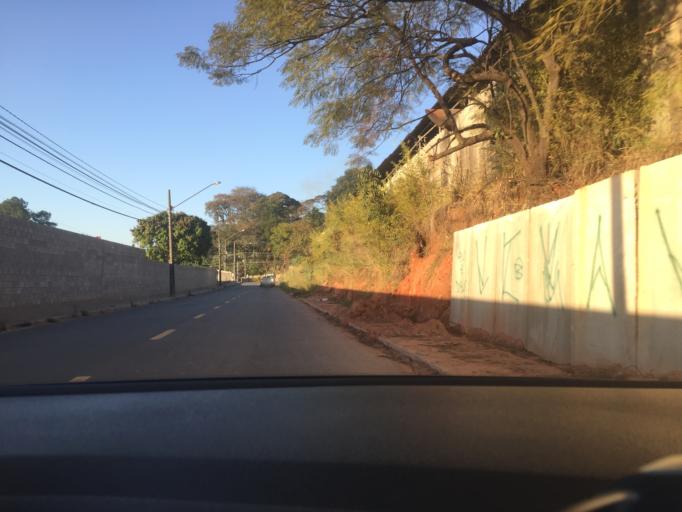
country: BR
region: Sao Paulo
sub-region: Varzea Paulista
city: Varzea Paulista
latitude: -23.2064
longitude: -46.8138
